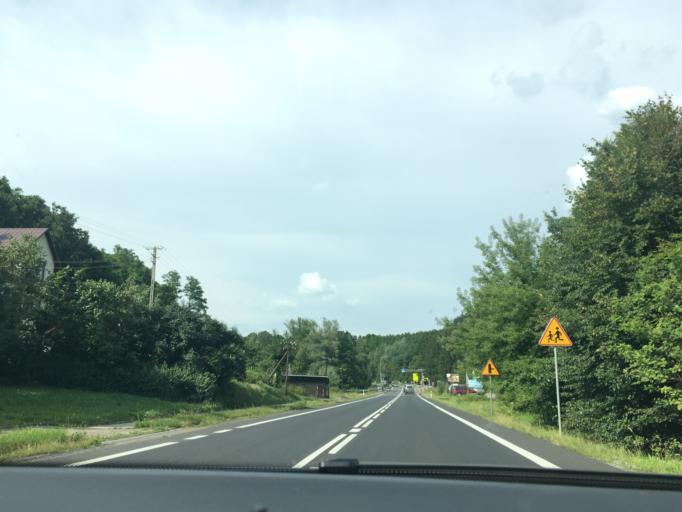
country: PL
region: Subcarpathian Voivodeship
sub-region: Powiat strzyzowski
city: Babica
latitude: 49.9189
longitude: 21.8778
